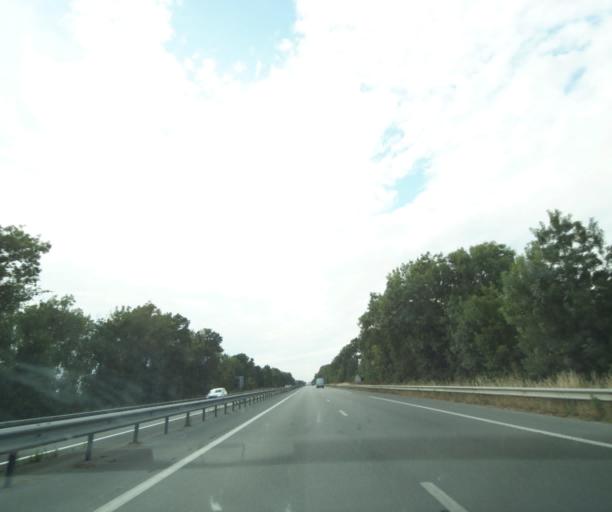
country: FR
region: Poitou-Charentes
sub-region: Departement de la Charente-Maritime
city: Chatelaillon-Plage
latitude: 46.0855
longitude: -1.0804
